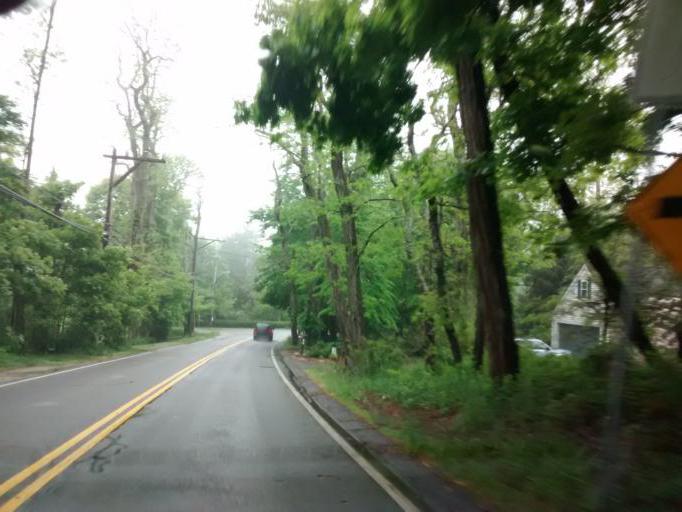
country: US
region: Massachusetts
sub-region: Barnstable County
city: Monument Beach
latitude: 41.7170
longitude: -70.6092
